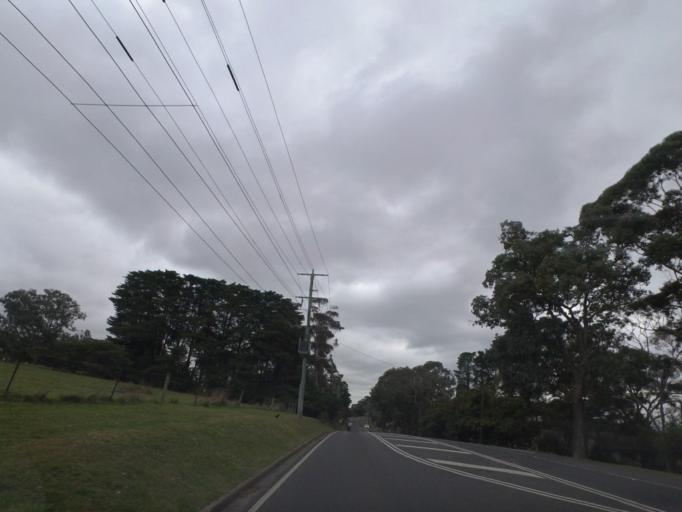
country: AU
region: Victoria
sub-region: Nillumbik
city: Diamond Creek
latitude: -37.6821
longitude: 145.1437
